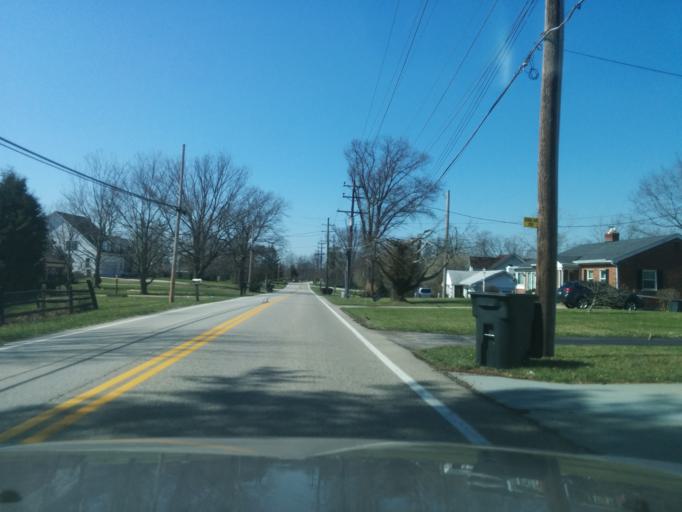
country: US
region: Ohio
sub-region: Hamilton County
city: Monfort Heights
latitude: 39.1817
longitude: -84.6111
